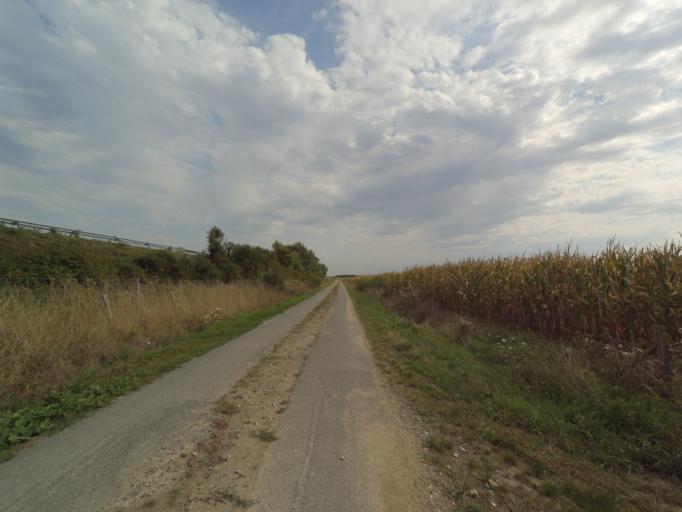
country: FR
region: Pays de la Loire
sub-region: Departement de la Vendee
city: Bouffere
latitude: 46.9862
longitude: -1.3799
